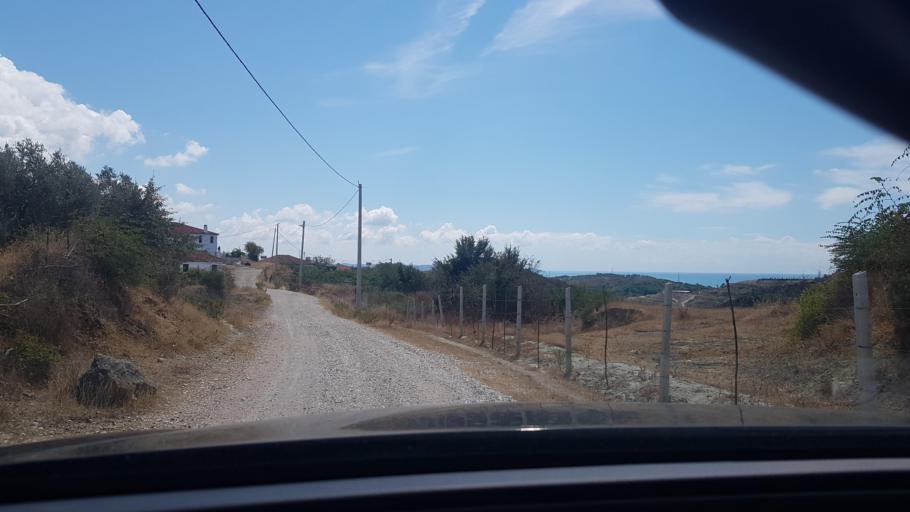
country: AL
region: Tirane
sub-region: Rrethi i Kavajes
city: Golem
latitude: 41.2841
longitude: 19.5467
